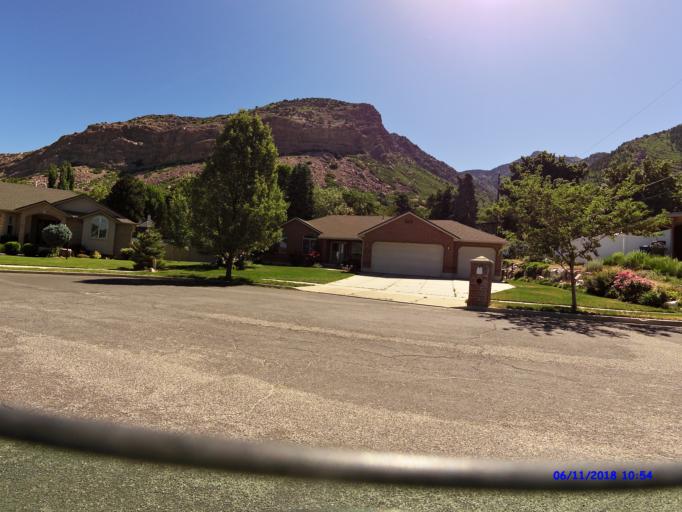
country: US
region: Utah
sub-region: Weber County
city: Ogden
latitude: 41.2170
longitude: -111.9312
